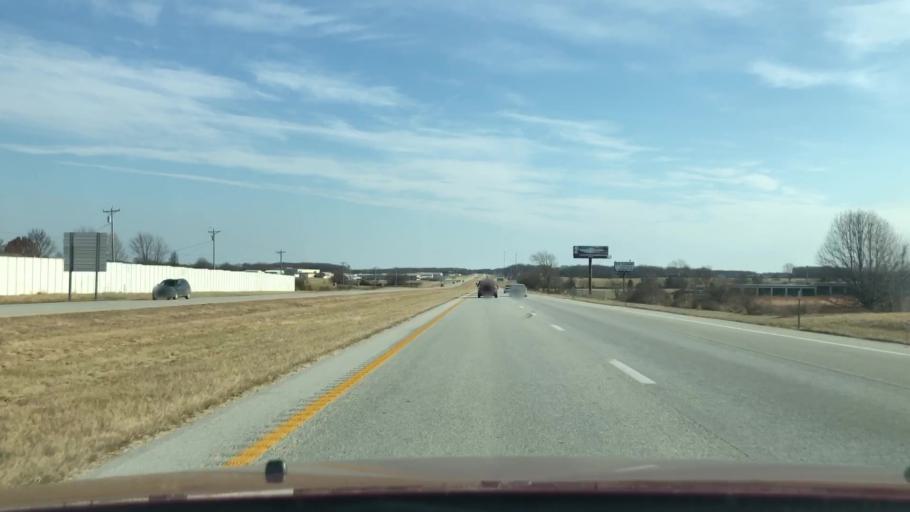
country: US
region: Missouri
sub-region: Webster County
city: Rogersville
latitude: 37.1118
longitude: -93.0499
